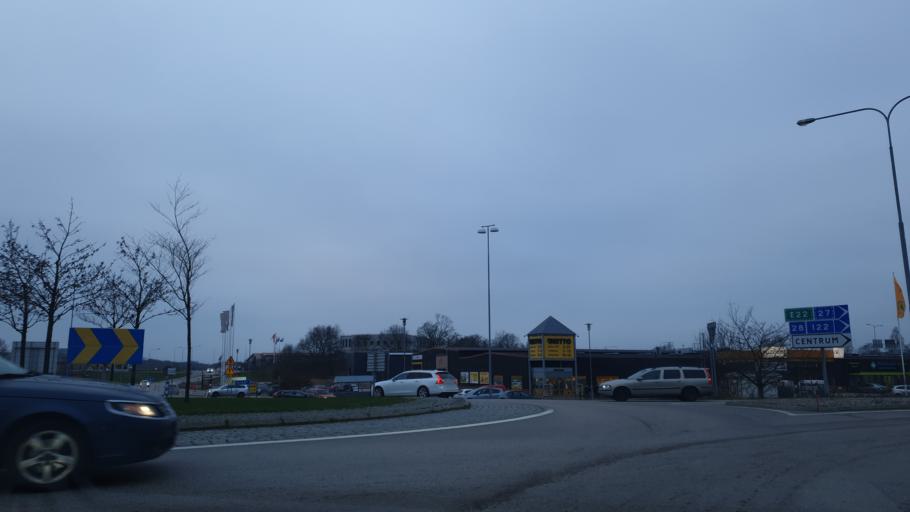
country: SE
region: Blekinge
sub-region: Karlskrona Kommun
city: Rodeby
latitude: 56.2022
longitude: 15.6410
